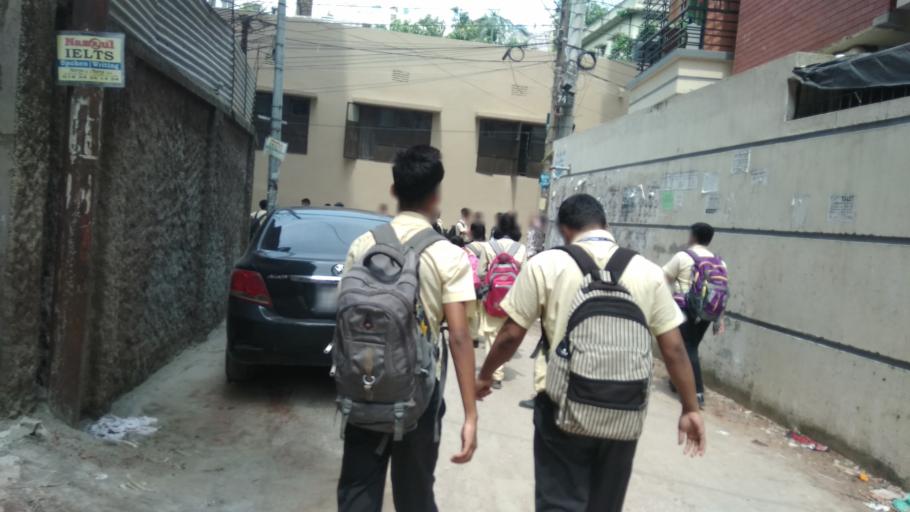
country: BD
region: Dhaka
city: Azimpur
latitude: 23.8049
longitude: 90.3668
